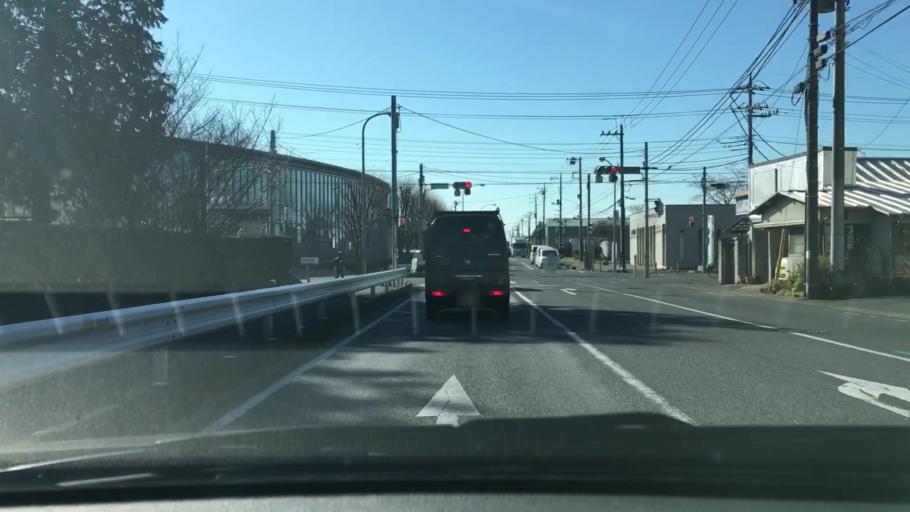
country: JP
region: Chiba
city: Narita
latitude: 35.7276
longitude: 140.3394
